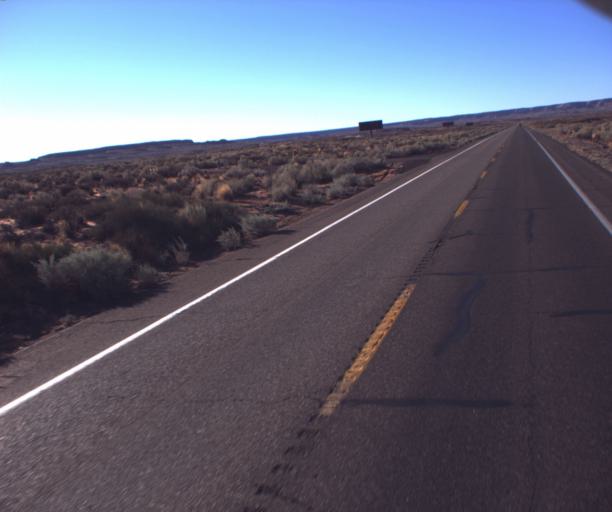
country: US
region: Arizona
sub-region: Coconino County
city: Page
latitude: 36.8667
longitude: -111.5037
